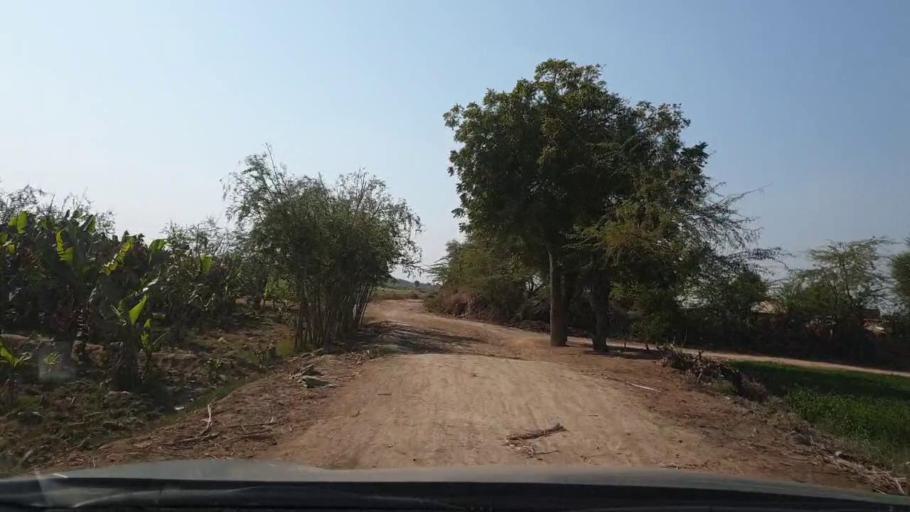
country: PK
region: Sindh
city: Mirpur Khas
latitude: 25.6019
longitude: 68.8617
